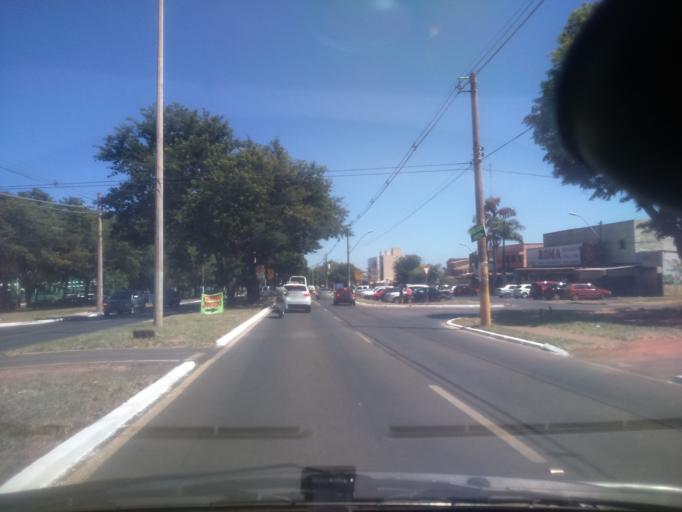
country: BR
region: Goias
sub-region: Luziania
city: Luziania
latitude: -16.0108
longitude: -48.0638
